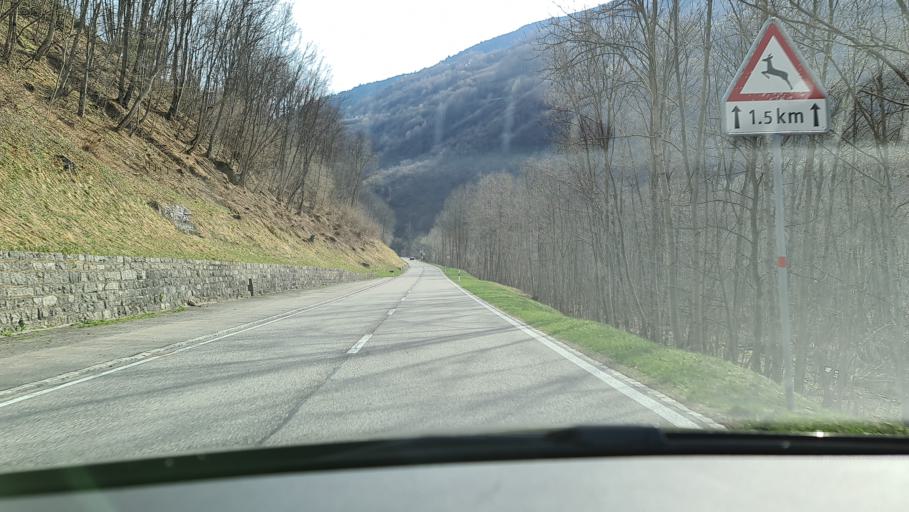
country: CH
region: Ticino
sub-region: Blenio District
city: Acquarossa
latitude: 46.5235
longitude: 8.9401
